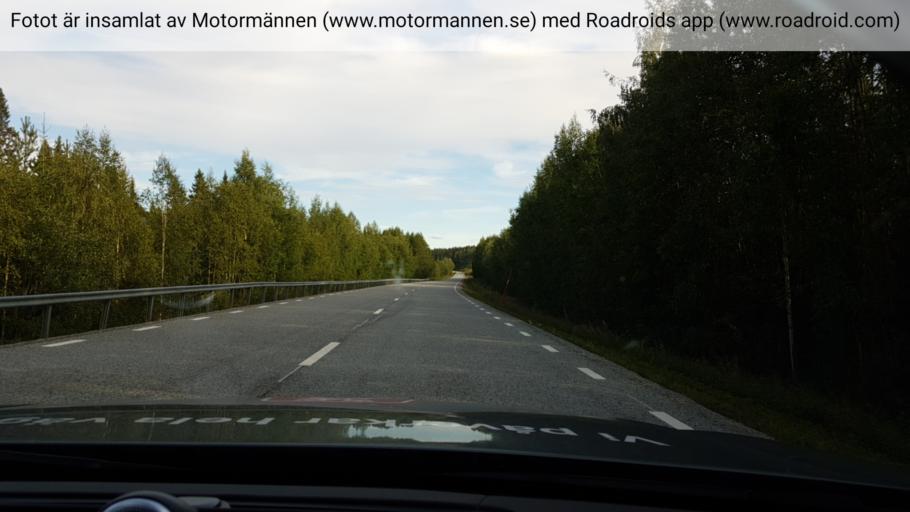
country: SE
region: Jaemtland
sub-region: Stroemsunds Kommun
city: Stroemsund
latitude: 64.1922
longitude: 15.6339
